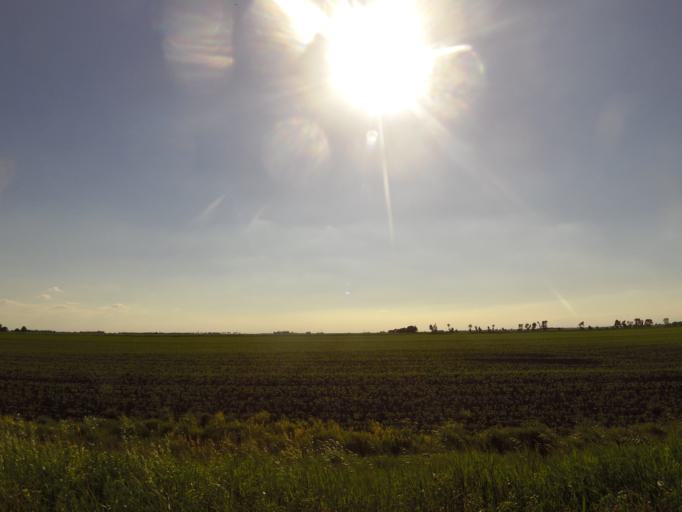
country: US
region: North Dakota
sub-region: Walsh County
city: Grafton
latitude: 48.4042
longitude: -97.2338
